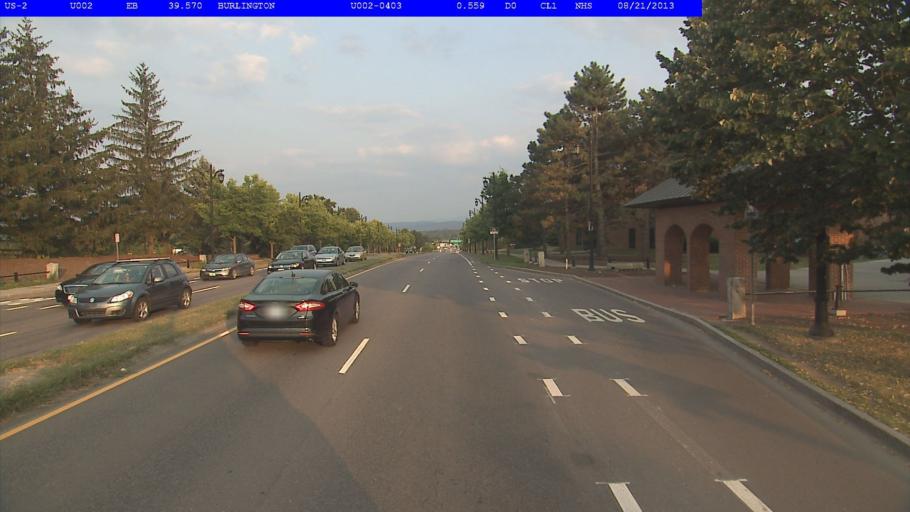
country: US
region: Vermont
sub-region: Chittenden County
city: Burlington
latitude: 44.4746
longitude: -73.1949
